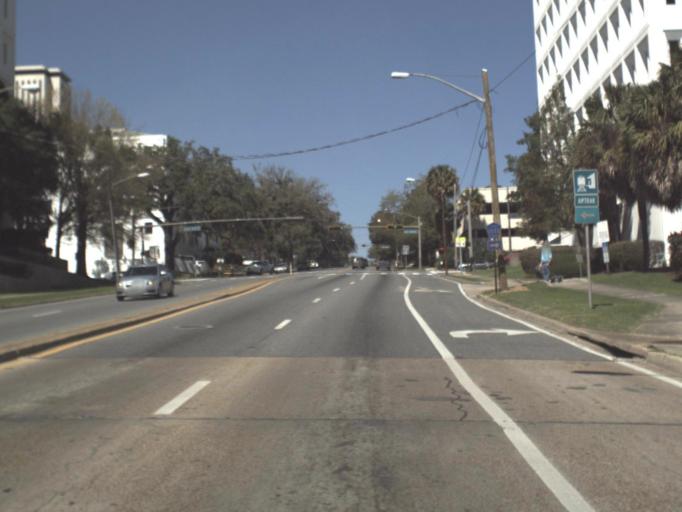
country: US
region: Florida
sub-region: Leon County
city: Tallahassee
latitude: 30.4345
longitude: -84.2806
